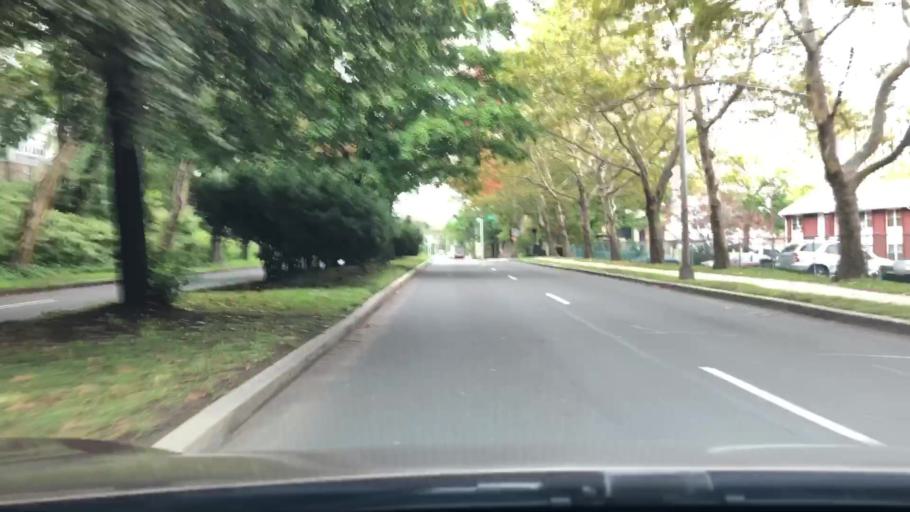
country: US
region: Connecticut
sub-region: Fairfield County
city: Norwalk
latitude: 41.0974
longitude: -73.4229
